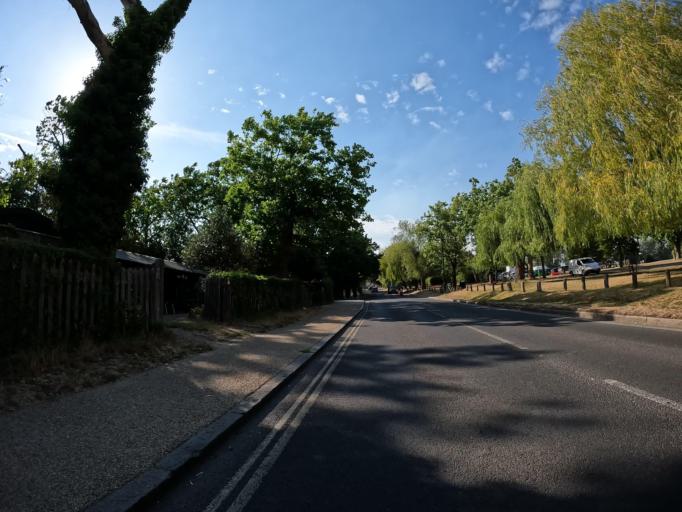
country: GB
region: England
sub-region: Greater London
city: Hadley Wood
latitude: 51.6771
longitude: -0.1628
